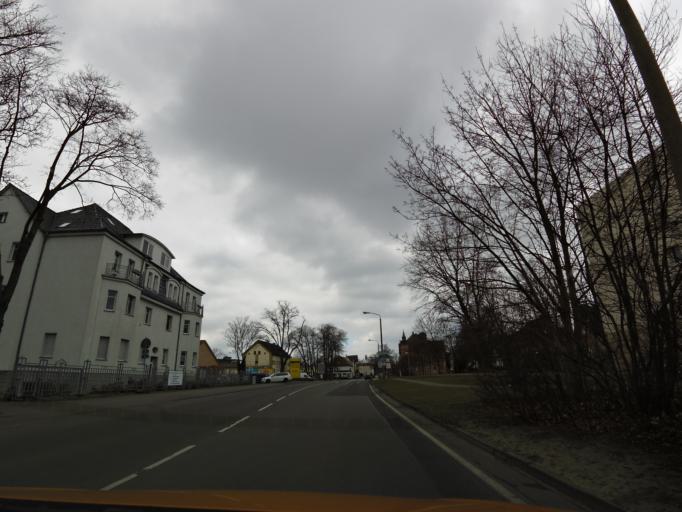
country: DE
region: Brandenburg
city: Rathenow
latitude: 52.6033
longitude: 12.3555
